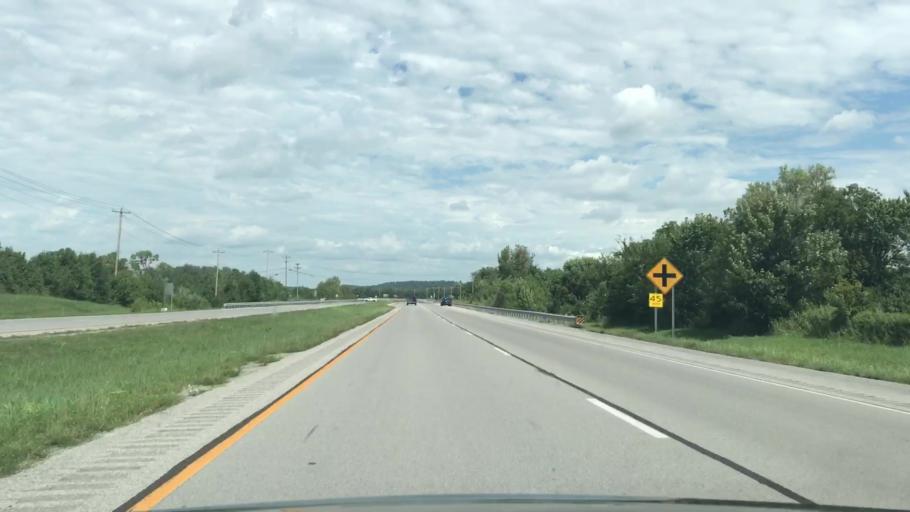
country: US
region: Kentucky
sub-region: Logan County
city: Russellville
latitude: 36.8523
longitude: -86.8633
